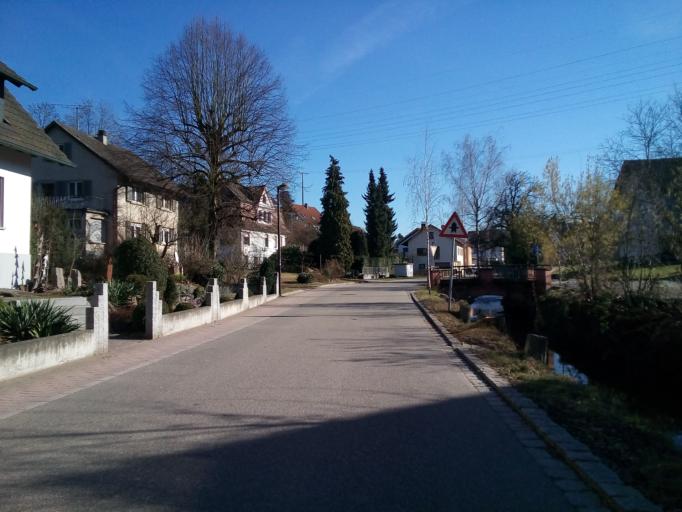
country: DE
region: Baden-Wuerttemberg
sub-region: Freiburg Region
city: Achern
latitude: 48.6210
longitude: 8.0549
